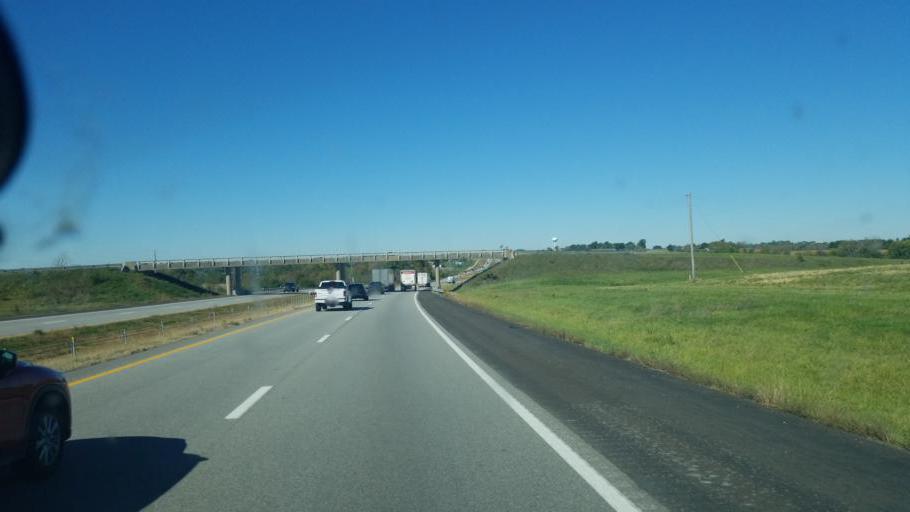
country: US
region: Missouri
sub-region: Lafayette County
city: Higginsville
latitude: 38.9936
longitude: -93.7102
